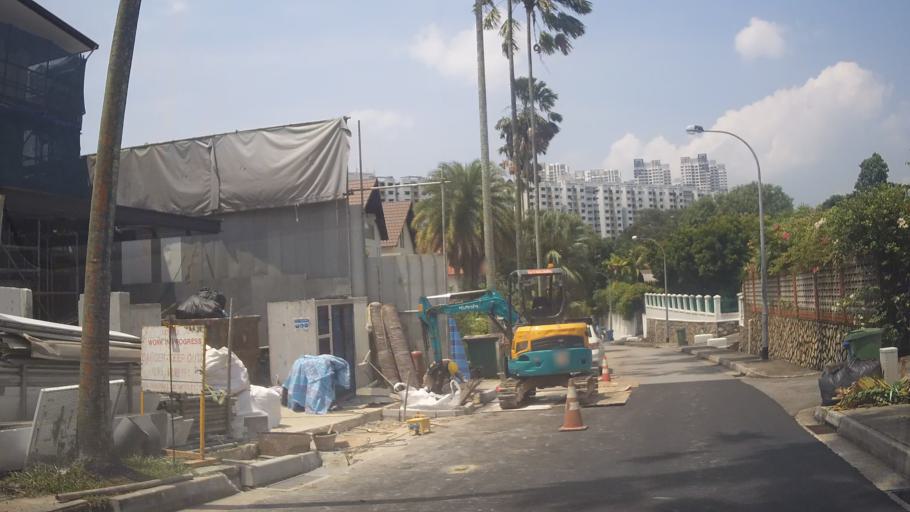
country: SG
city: Singapore
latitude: 1.3155
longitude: 103.7884
